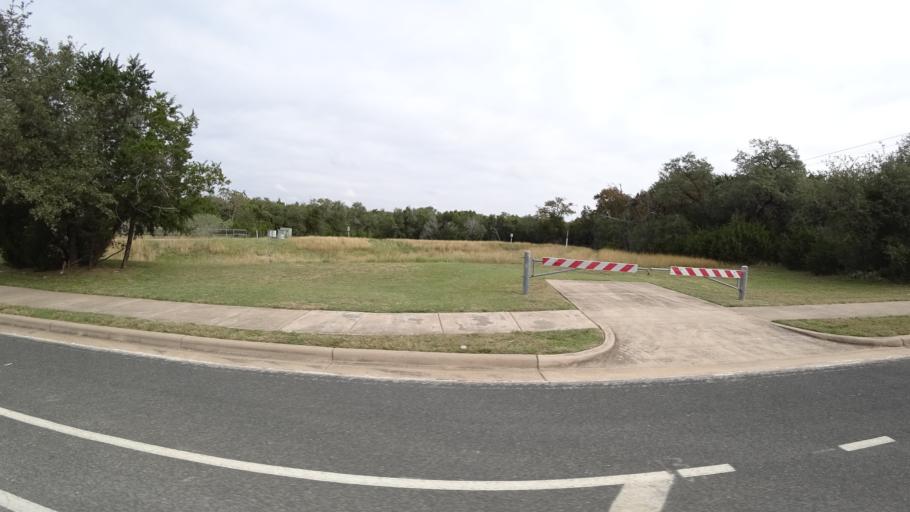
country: US
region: Texas
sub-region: Travis County
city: Shady Hollow
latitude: 30.1951
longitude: -97.8936
